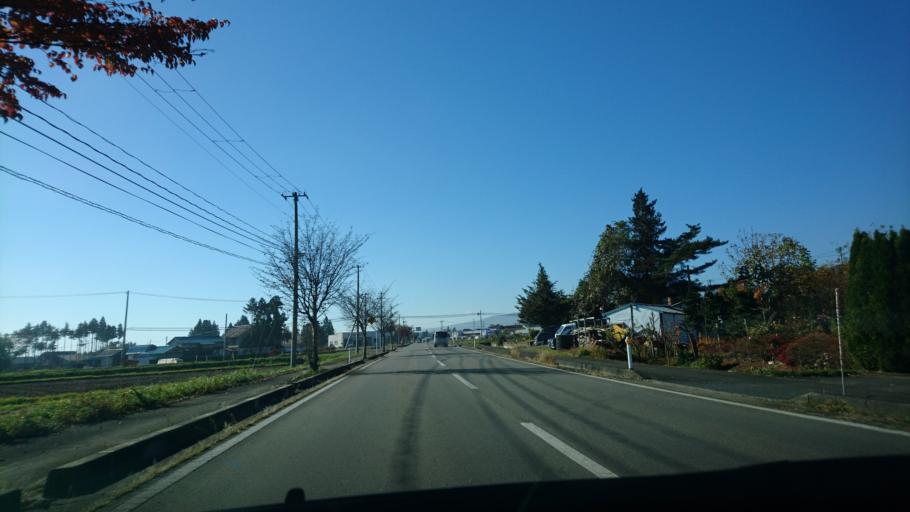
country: JP
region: Iwate
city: Mizusawa
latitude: 39.1345
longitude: 141.0679
